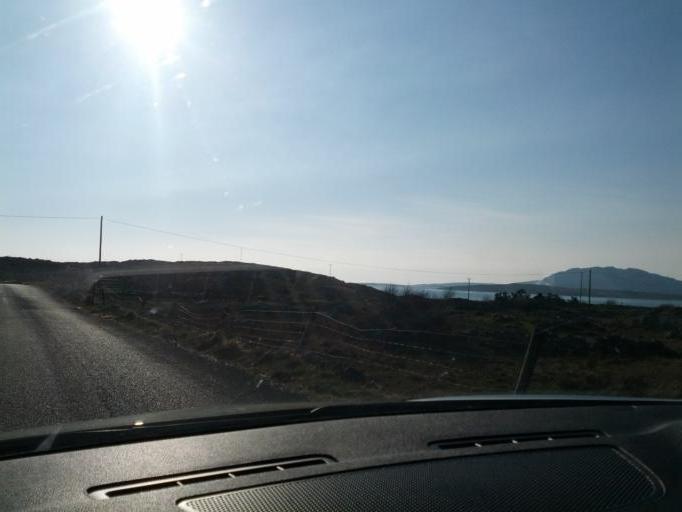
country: IE
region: Connaught
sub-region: County Galway
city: Clifden
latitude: 53.3716
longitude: -9.8530
